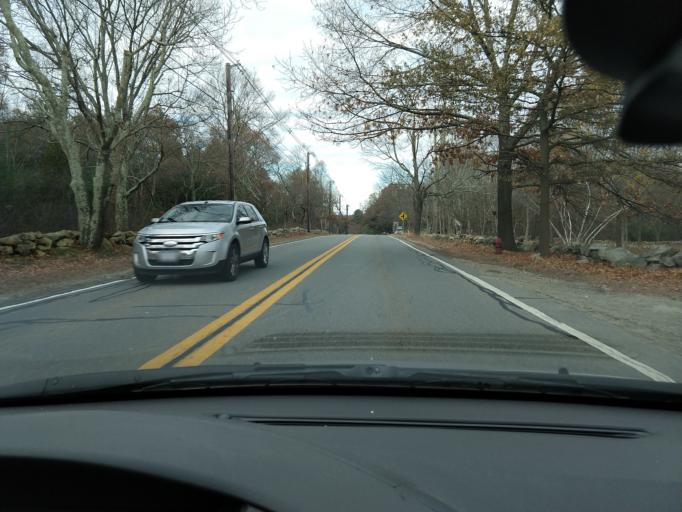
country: US
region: Massachusetts
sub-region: Middlesex County
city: Lincoln
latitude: 42.4489
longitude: -71.2752
